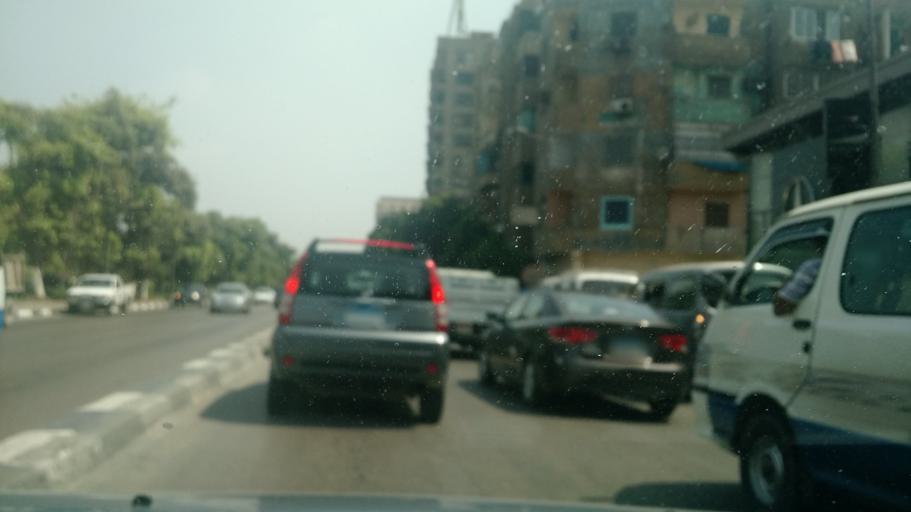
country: EG
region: Al Jizah
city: Al Jizah
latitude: 30.0195
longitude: 31.2295
